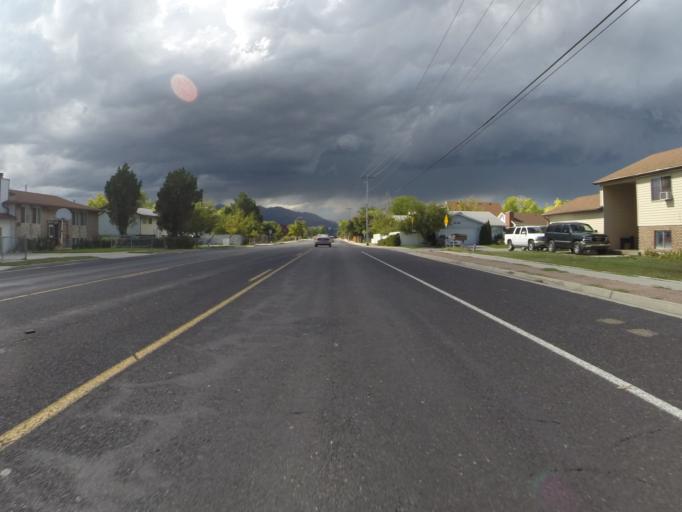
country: US
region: Utah
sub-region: Salt Lake County
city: West Valley City
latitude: 40.7039
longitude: -112.0032
